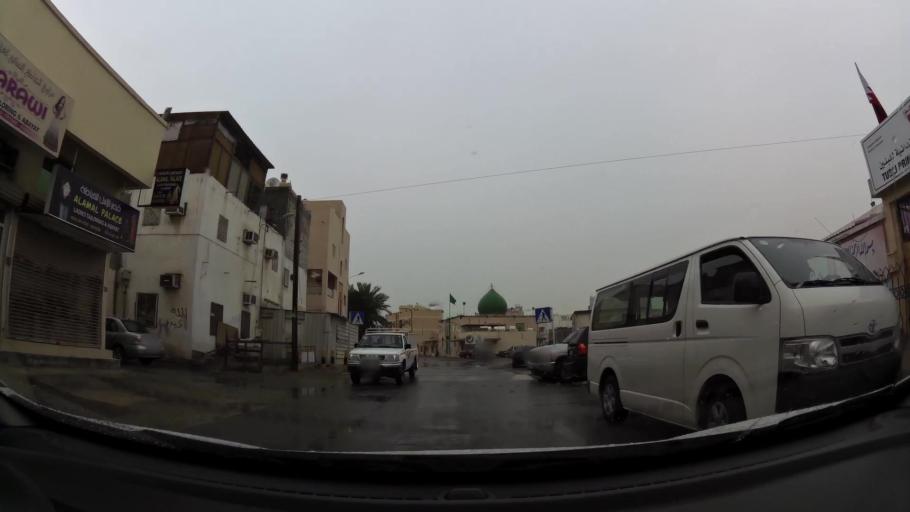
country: BH
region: Northern
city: Madinat `Isa
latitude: 26.1814
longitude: 50.5509
